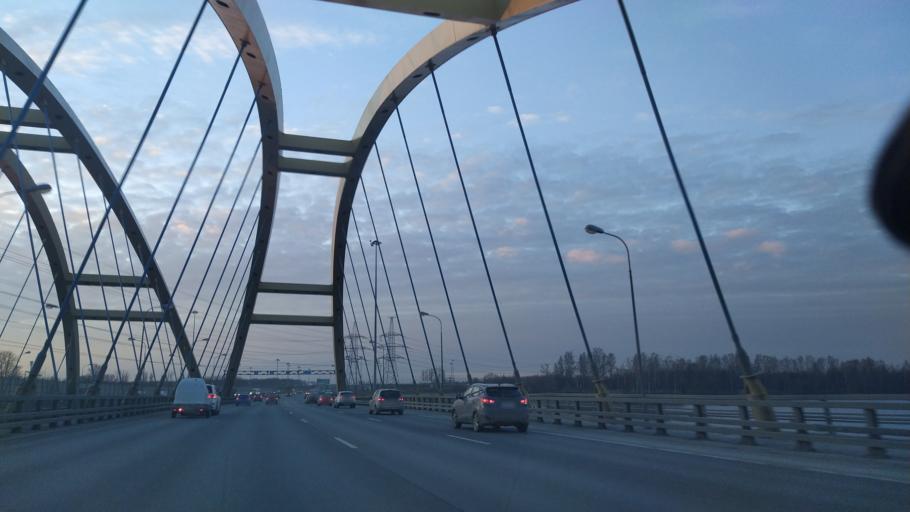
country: RU
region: St.-Petersburg
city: Krasnogvargeisky
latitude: 59.9850
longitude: 30.4942
